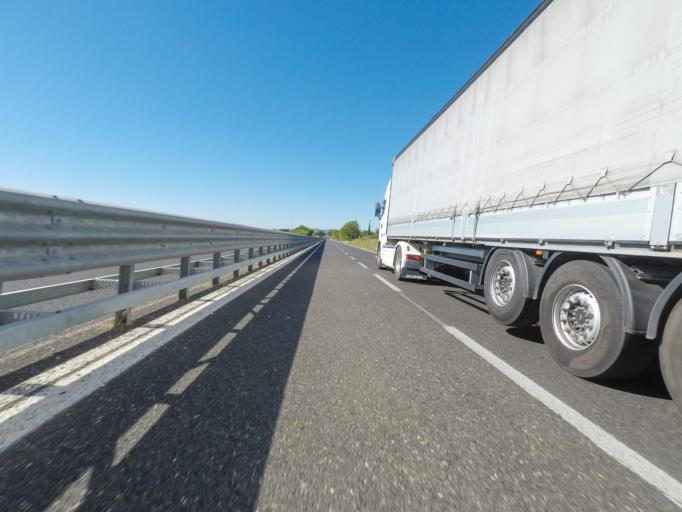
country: IT
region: Latium
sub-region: Provincia di Viterbo
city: Pescia Romana
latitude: 42.3918
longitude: 11.5356
